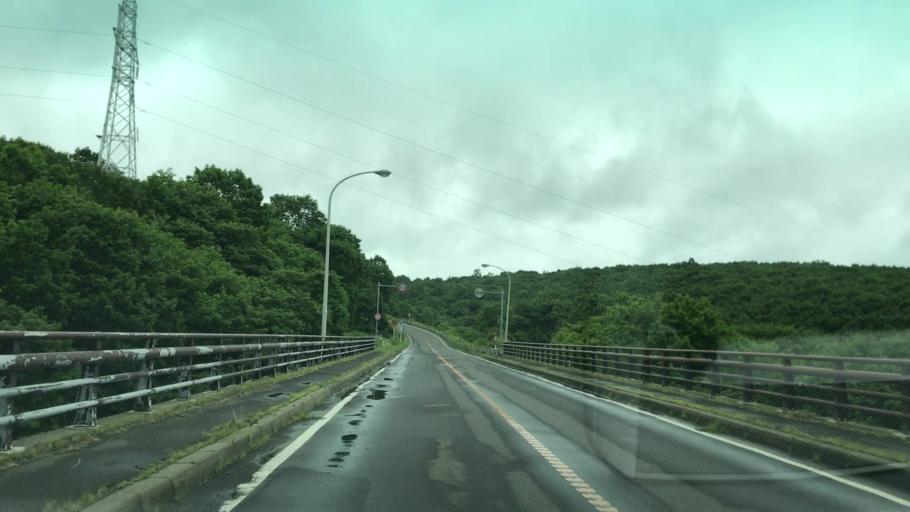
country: JP
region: Hokkaido
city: Muroran
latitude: 42.3808
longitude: 140.9681
